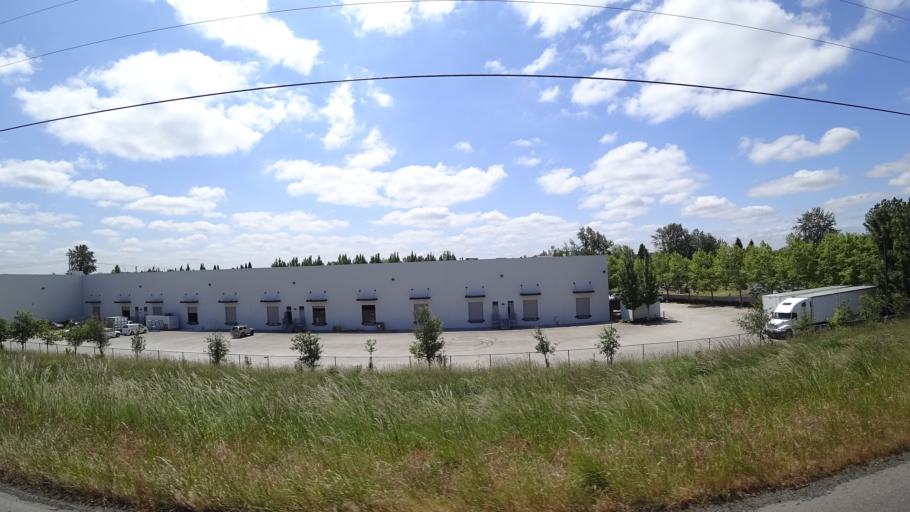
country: US
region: Washington
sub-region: Clark County
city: Mill Plain
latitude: 45.5694
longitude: -122.5363
